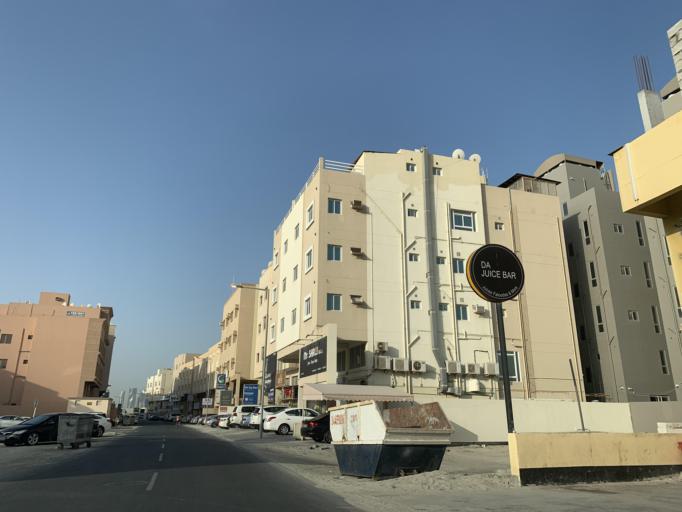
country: BH
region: Muharraq
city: Al Muharraq
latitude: 26.2796
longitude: 50.5967
